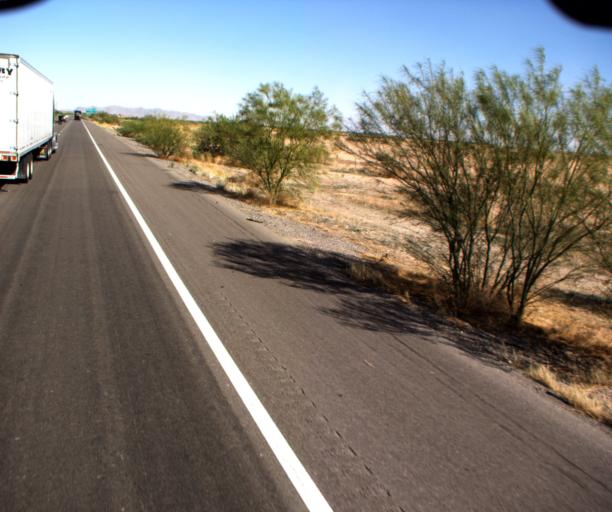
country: US
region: Arizona
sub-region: Pinal County
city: Casa Grande
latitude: 32.8279
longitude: -111.8754
